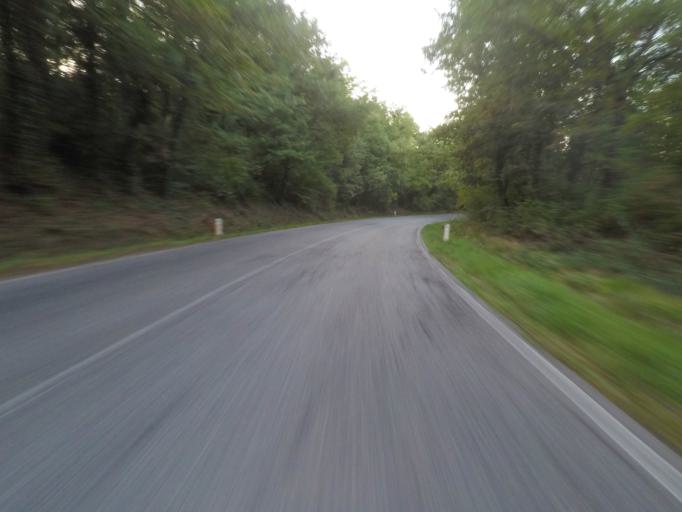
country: IT
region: Tuscany
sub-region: Provincia di Siena
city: Torrita di Siena
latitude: 43.1414
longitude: 11.7361
